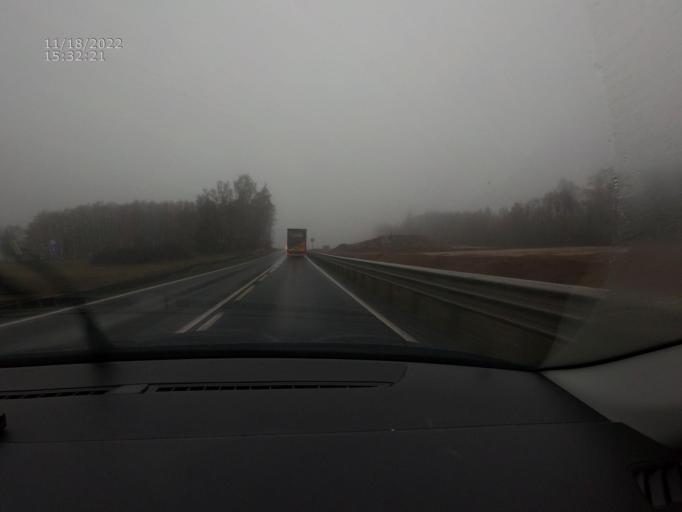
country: CZ
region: Central Bohemia
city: Milin
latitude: 49.6615
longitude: 14.0589
